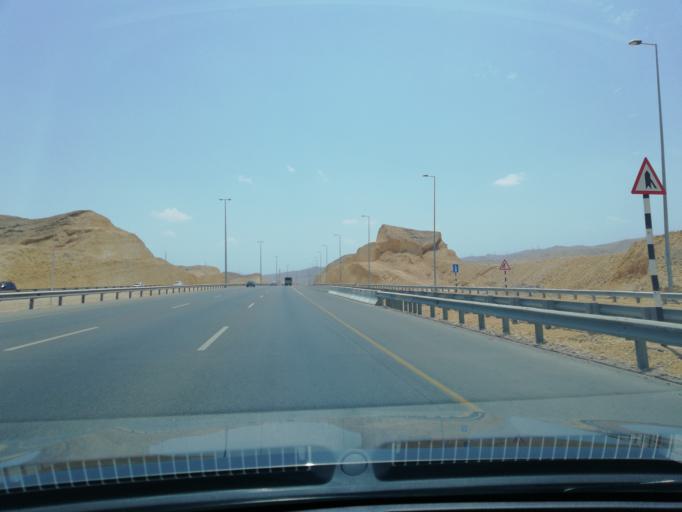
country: OM
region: Muhafazat Masqat
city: As Sib al Jadidah
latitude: 23.5588
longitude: 58.2215
